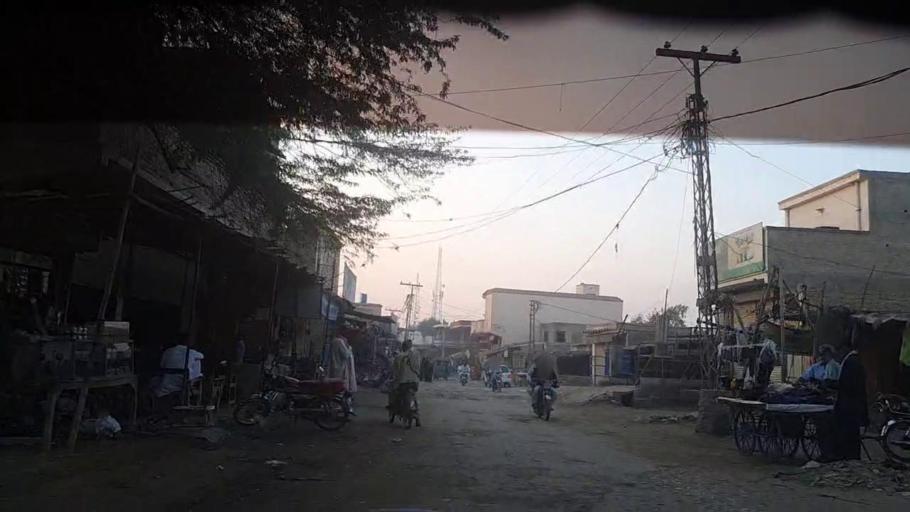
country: PK
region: Sindh
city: Ranipur
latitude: 27.2845
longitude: 68.5109
